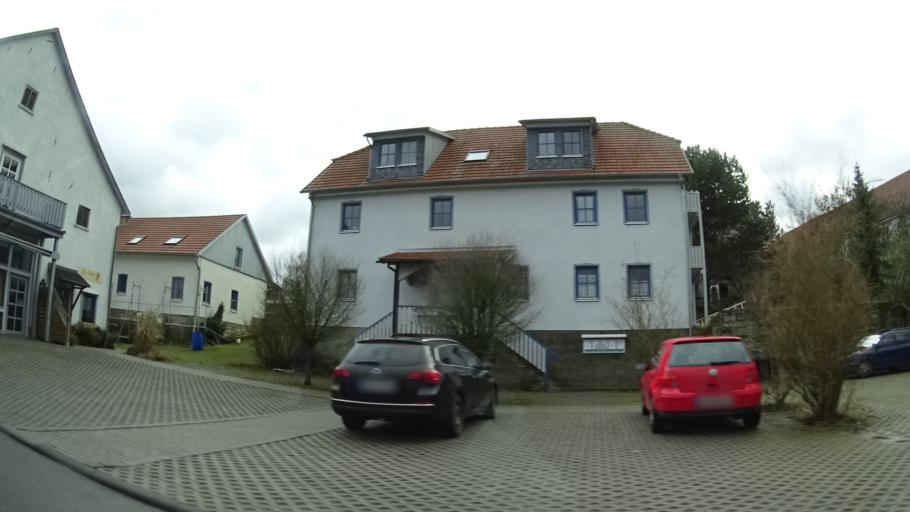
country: DE
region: Thuringia
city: Meiningen
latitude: 50.5596
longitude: 10.3882
